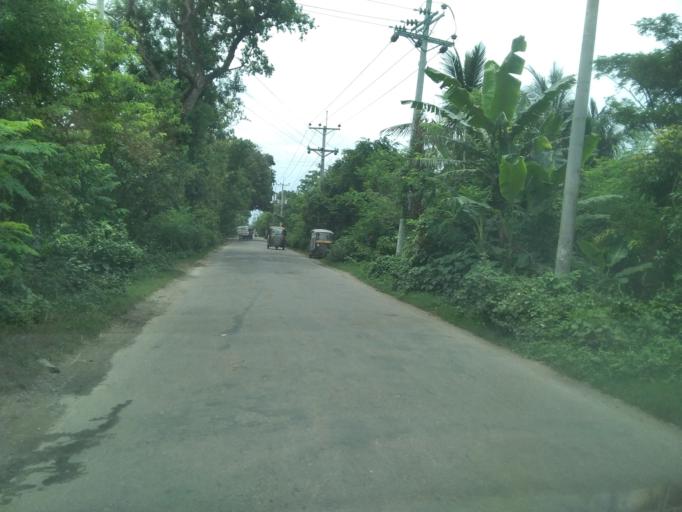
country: IN
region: West Bengal
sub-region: North 24 Parganas
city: Taki
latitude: 22.5748
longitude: 88.9995
